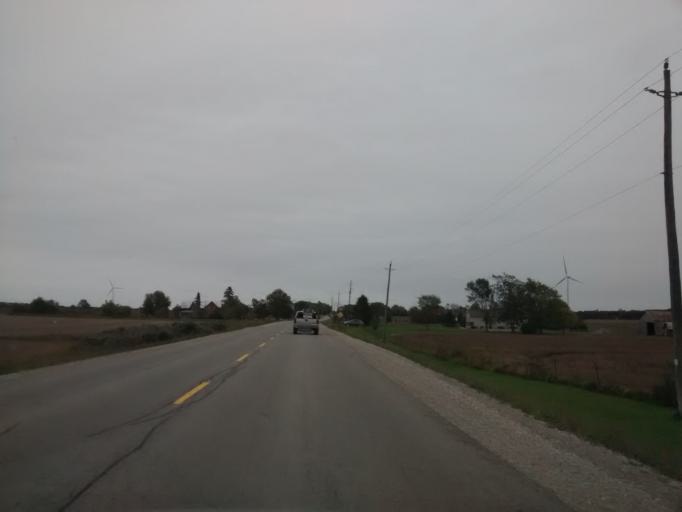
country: CA
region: Ontario
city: Hamilton
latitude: 42.8632
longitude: -79.7622
